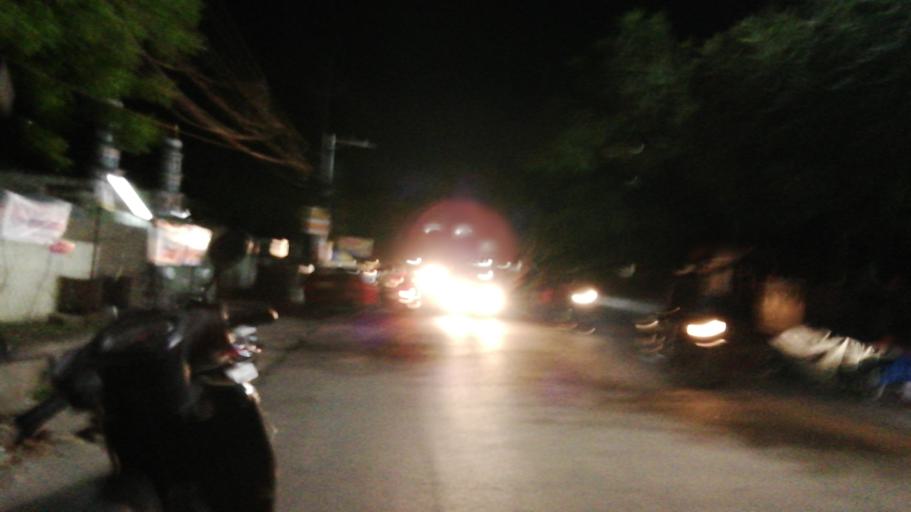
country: IN
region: Telangana
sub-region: Hyderabad
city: Hyderabad
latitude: 17.4311
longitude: 78.4320
